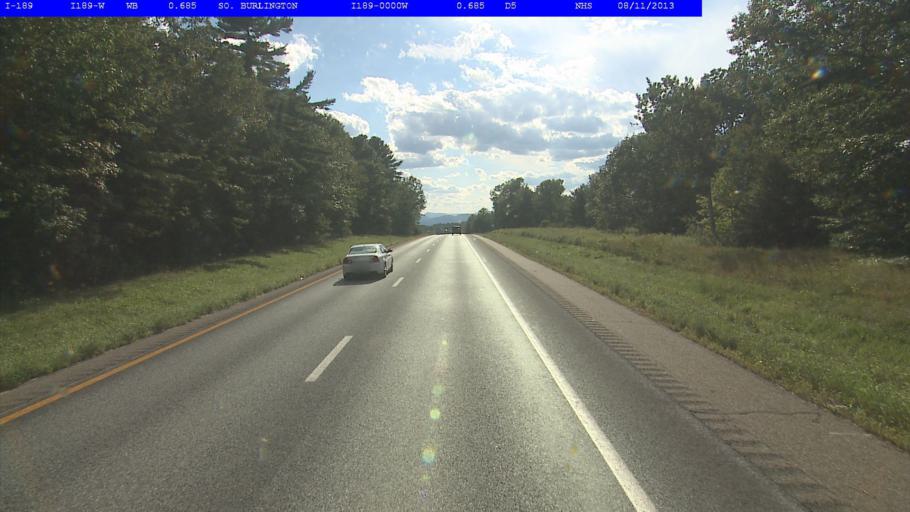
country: US
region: Vermont
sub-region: Chittenden County
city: Burlington
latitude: 44.4501
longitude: -73.1968
